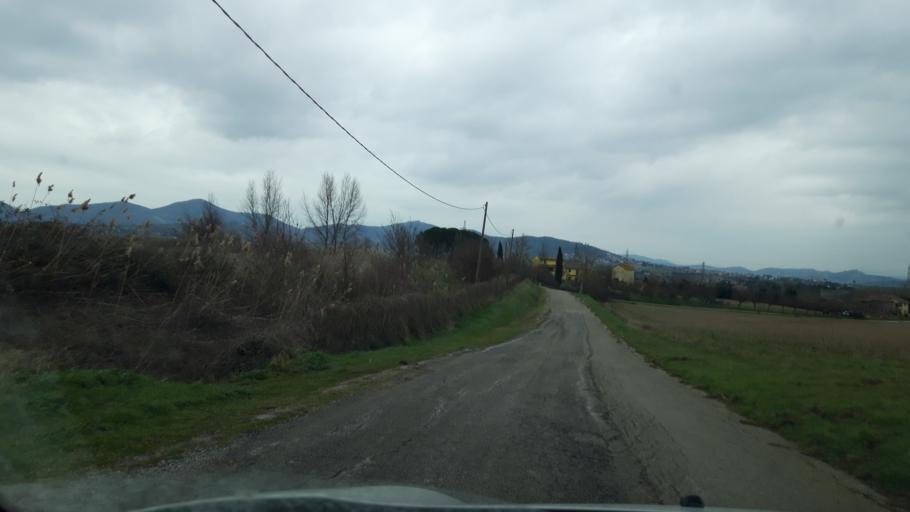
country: IT
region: Umbria
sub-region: Provincia di Perugia
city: Fontignano
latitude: 42.9926
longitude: 12.1803
